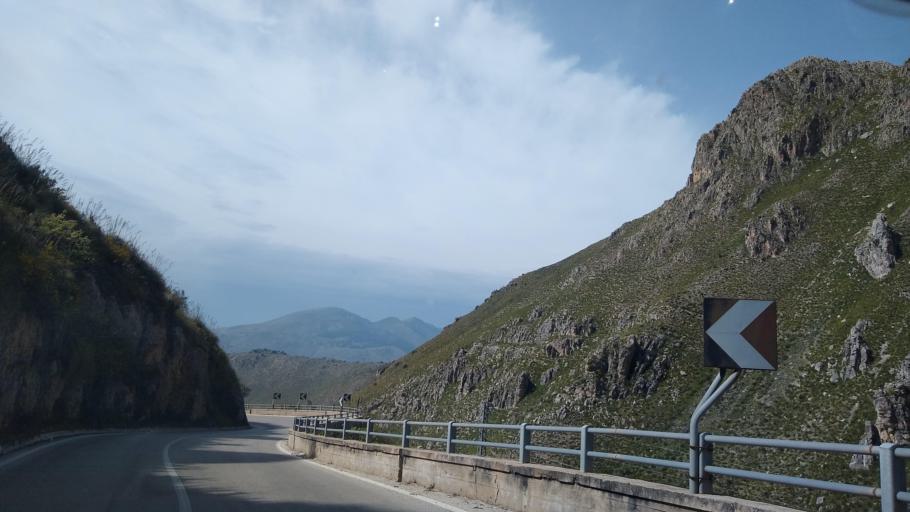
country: IT
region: Sicily
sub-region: Palermo
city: Montelepre
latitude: 38.0515
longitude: 13.1857
